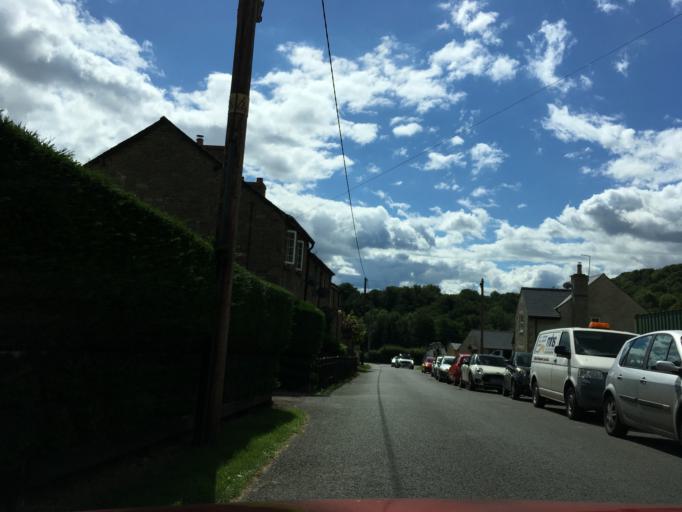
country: GB
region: England
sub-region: Gloucestershire
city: Bream
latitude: 51.7447
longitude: -2.5587
